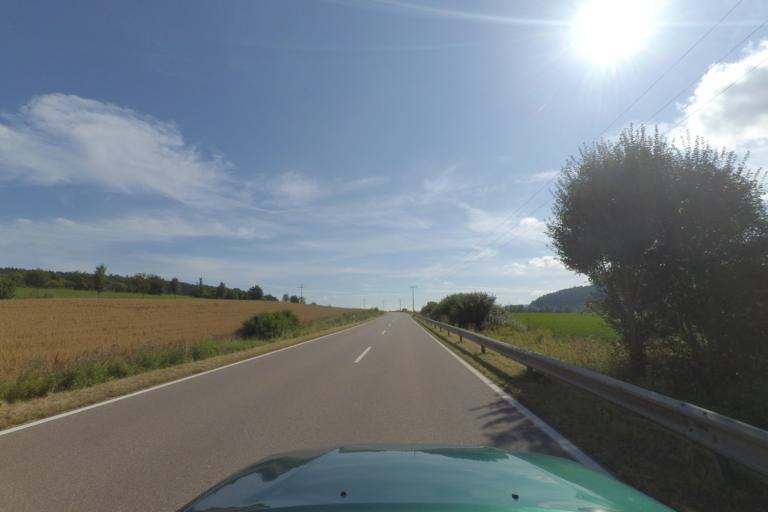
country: DE
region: Bavaria
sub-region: Lower Bavaria
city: Saal
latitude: 48.9166
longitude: 11.9614
